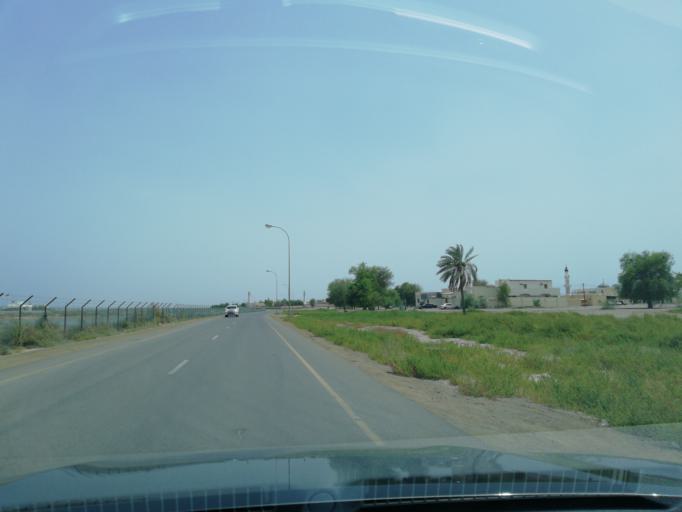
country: OM
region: Al Batinah
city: Shinas
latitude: 24.7505
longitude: 56.4674
